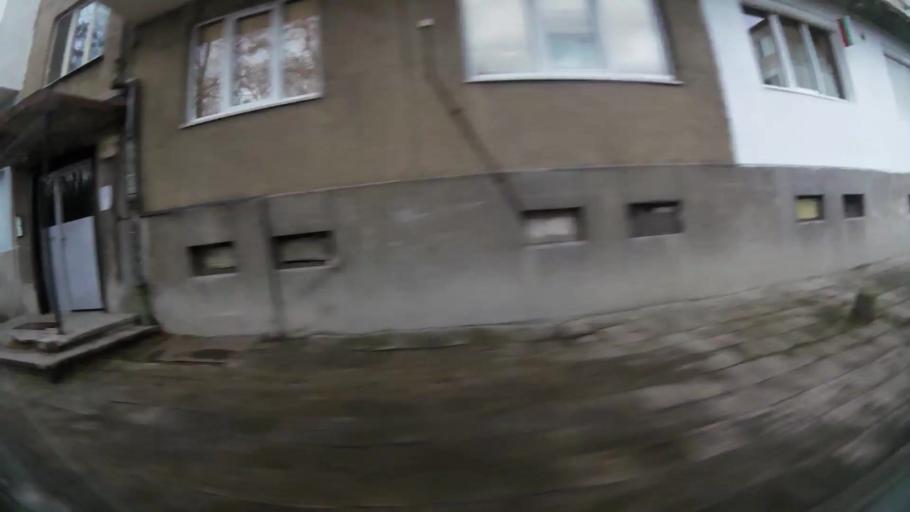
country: BG
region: Sofia-Capital
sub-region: Stolichna Obshtina
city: Sofia
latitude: 42.7356
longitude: 23.3023
